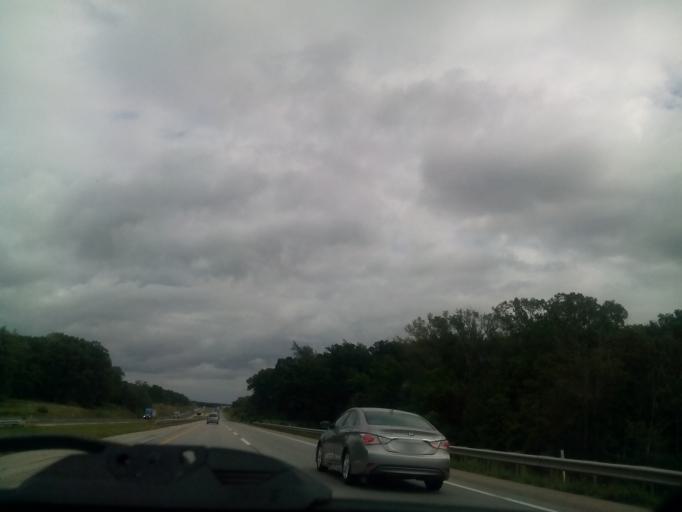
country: US
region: Indiana
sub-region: Steuben County
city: Fremont
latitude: 41.7102
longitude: -84.9397
